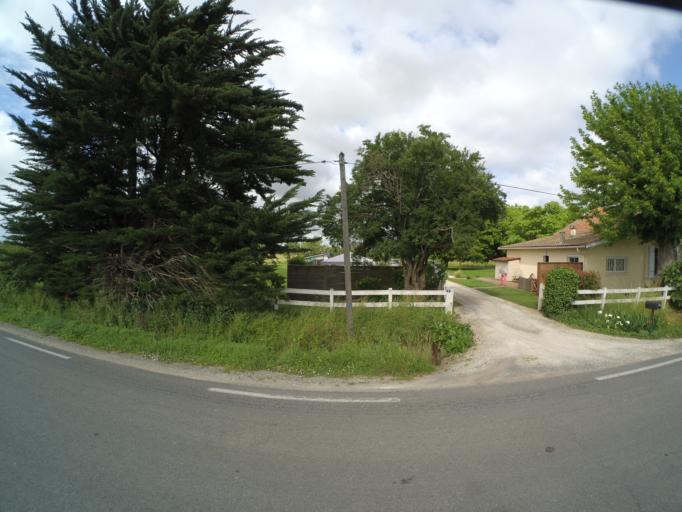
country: FR
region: Aquitaine
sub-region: Departement de la Gironde
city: Saint-Louis-de-Montferrand
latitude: 44.9747
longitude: -0.5585
